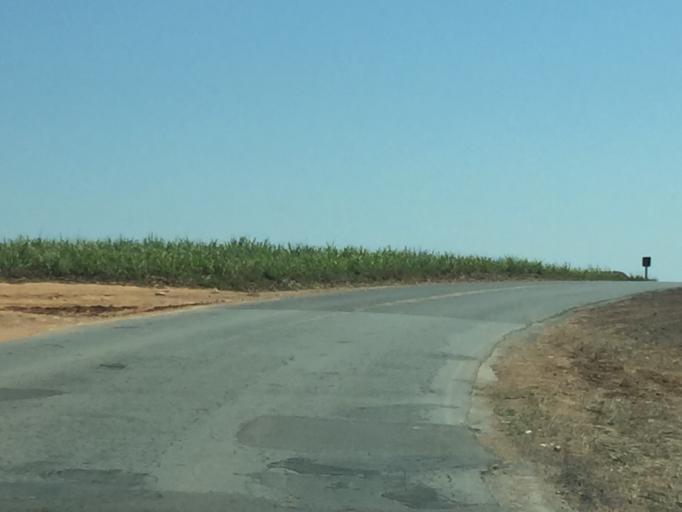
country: BR
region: Sao Paulo
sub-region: Itapira
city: Itapira
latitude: -22.3974
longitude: -46.8576
